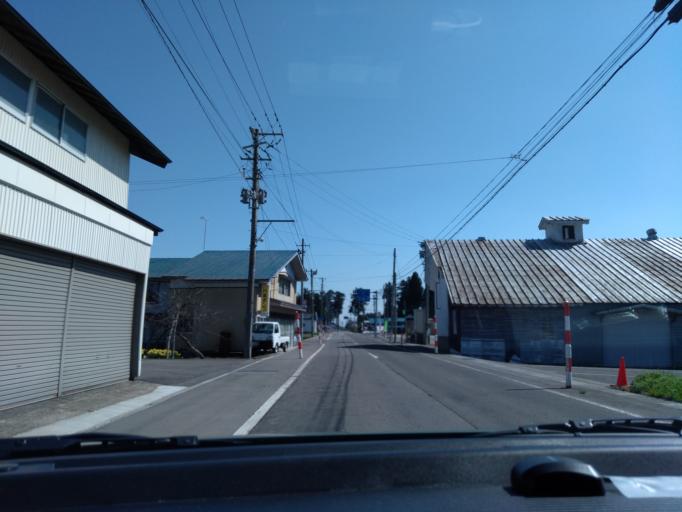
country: JP
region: Akita
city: Kakunodatemachi
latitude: 39.5544
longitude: 140.5860
